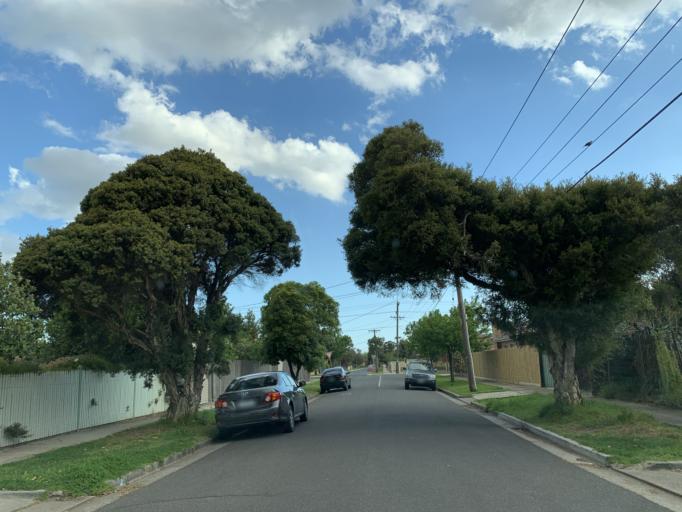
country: AU
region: Victoria
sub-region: Brimbank
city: Albion
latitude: -37.7685
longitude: 144.8411
